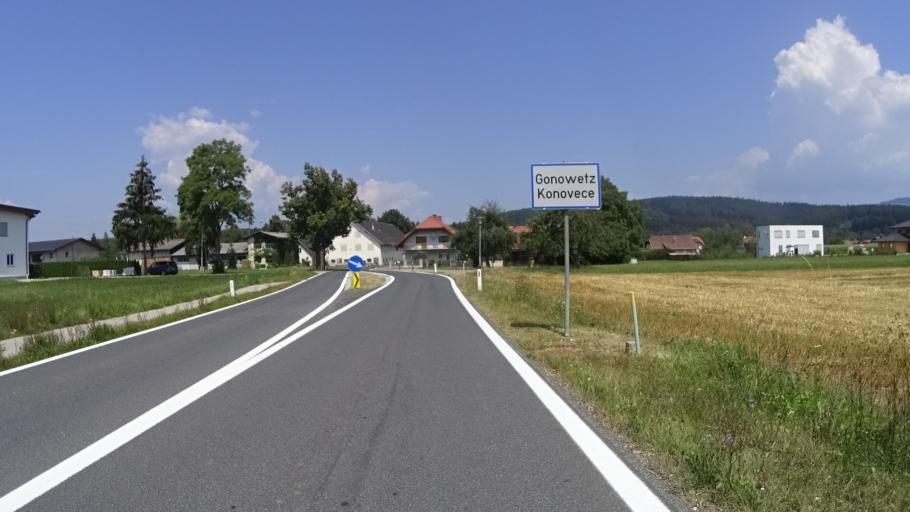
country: AT
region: Carinthia
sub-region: Politischer Bezirk Volkermarkt
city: Feistritz ob Bleiburg
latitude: 46.5723
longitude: 14.7709
